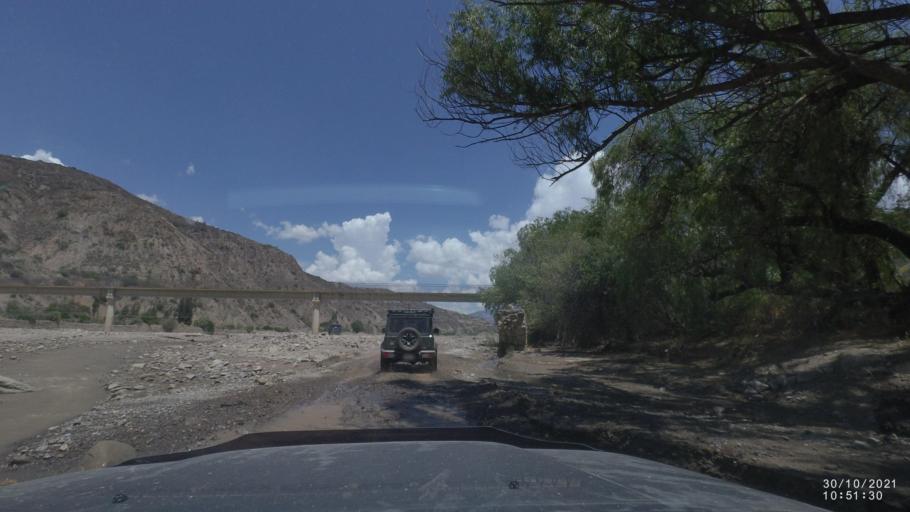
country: BO
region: Cochabamba
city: Sipe Sipe
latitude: -17.5540
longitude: -66.4743
